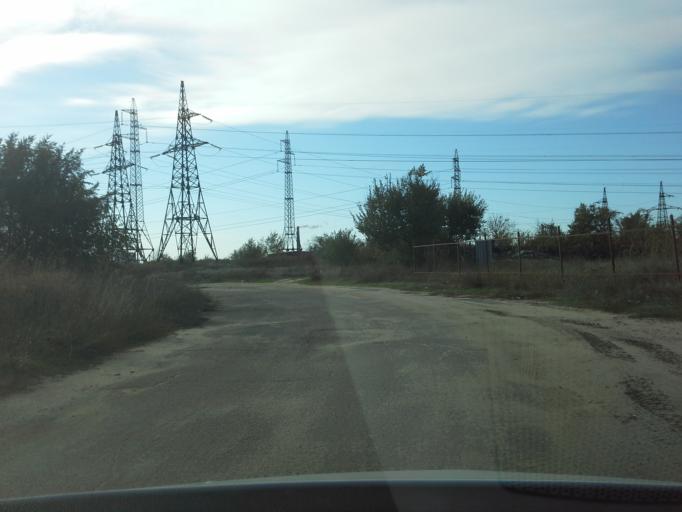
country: RU
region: Volgograd
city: Vodstroy
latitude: 48.8384
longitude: 44.6290
